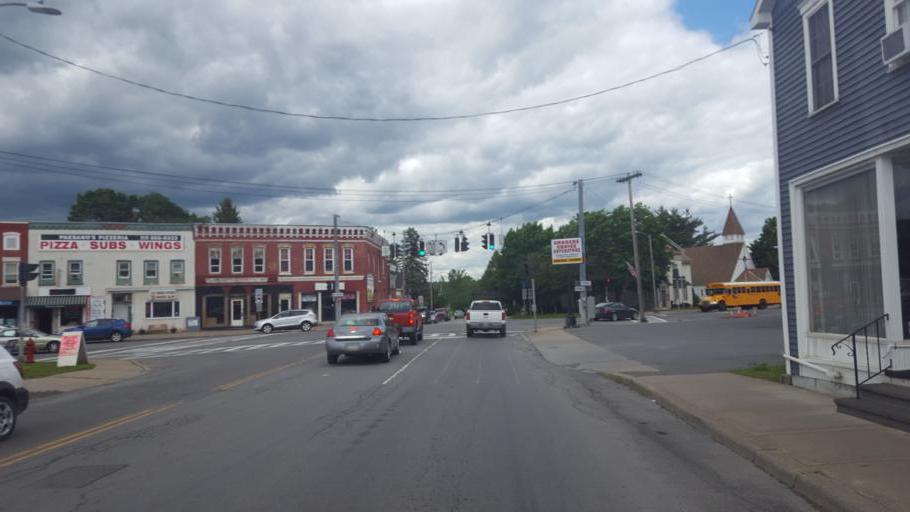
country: US
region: New York
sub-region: Herkimer County
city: Mohawk
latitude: 43.0110
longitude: -75.0044
